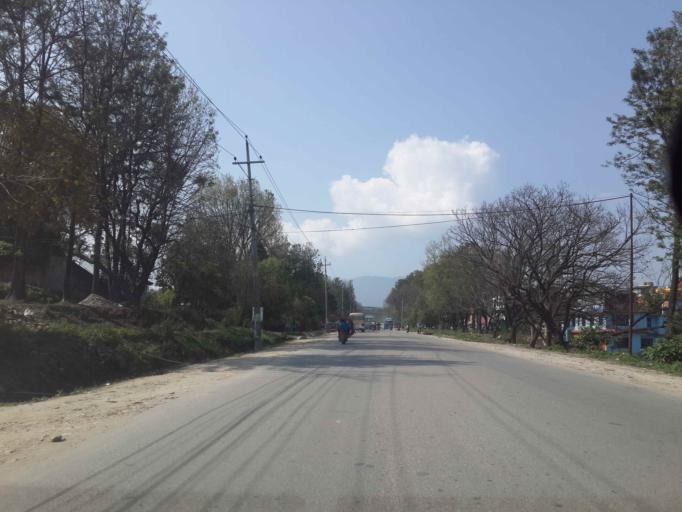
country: NP
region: Central Region
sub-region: Bagmati Zone
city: Kathmandu
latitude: 27.7327
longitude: 85.3437
